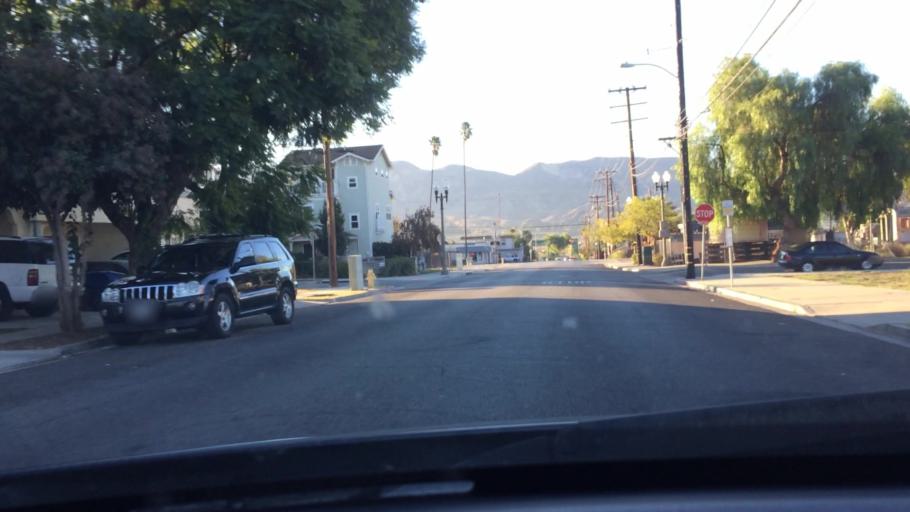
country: US
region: California
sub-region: Ventura County
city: Fillmore
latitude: 34.4002
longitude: -118.9089
